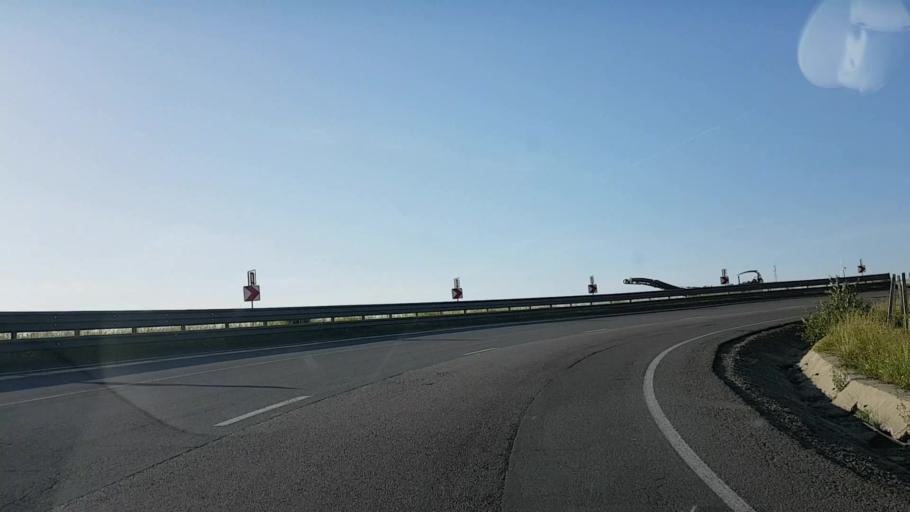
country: RO
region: Bistrita-Nasaud
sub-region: Comuna Lunca Ilvei
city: Lunca Ilvei
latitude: 47.2476
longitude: 25.0202
